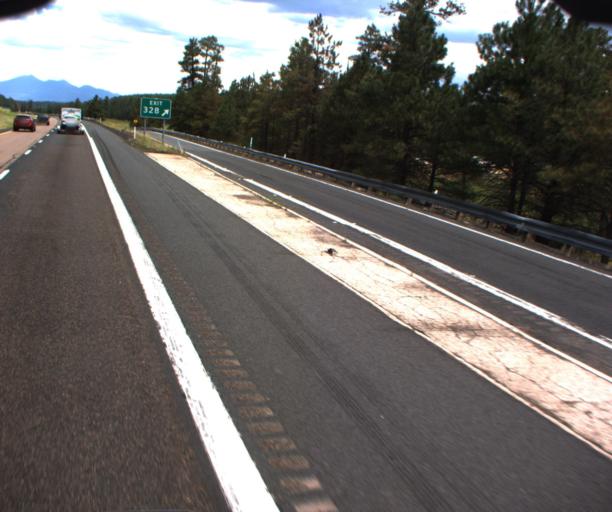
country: US
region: Arizona
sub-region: Coconino County
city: Mountainaire
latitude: 35.0154
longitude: -111.6846
